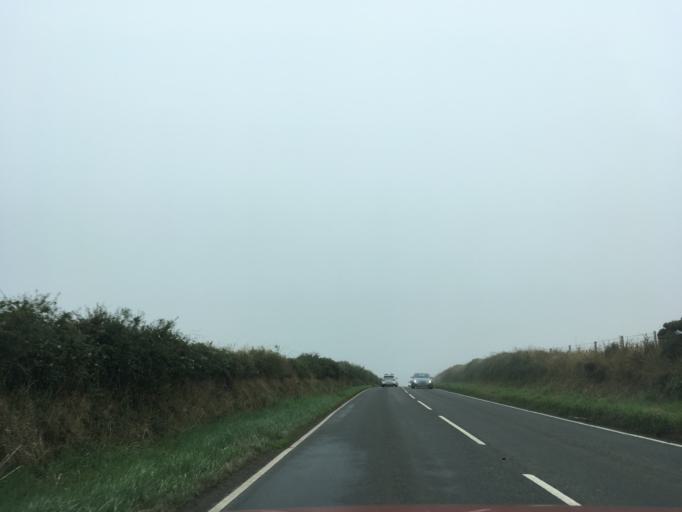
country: GB
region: Wales
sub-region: Pembrokeshire
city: Llanrhian
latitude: 51.8712
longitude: -5.1511
